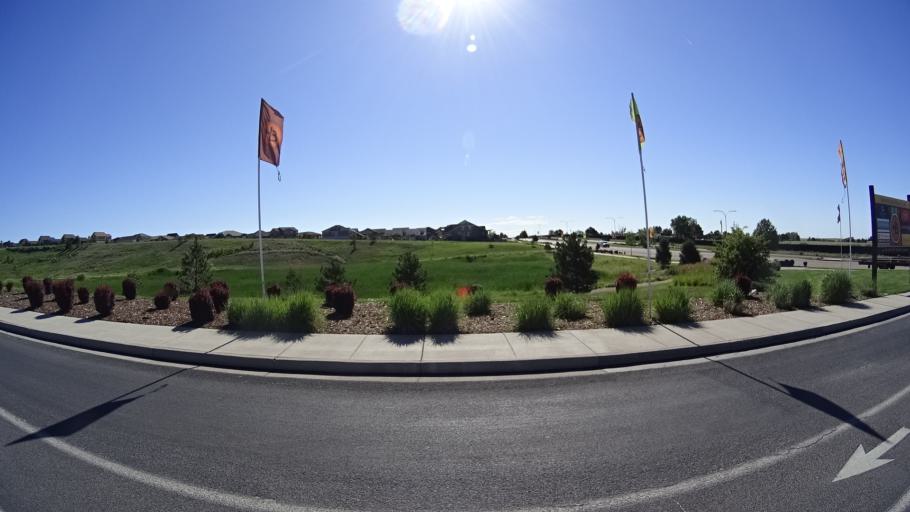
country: US
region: Colorado
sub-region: El Paso County
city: Cimarron Hills
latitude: 38.9272
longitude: -104.6827
